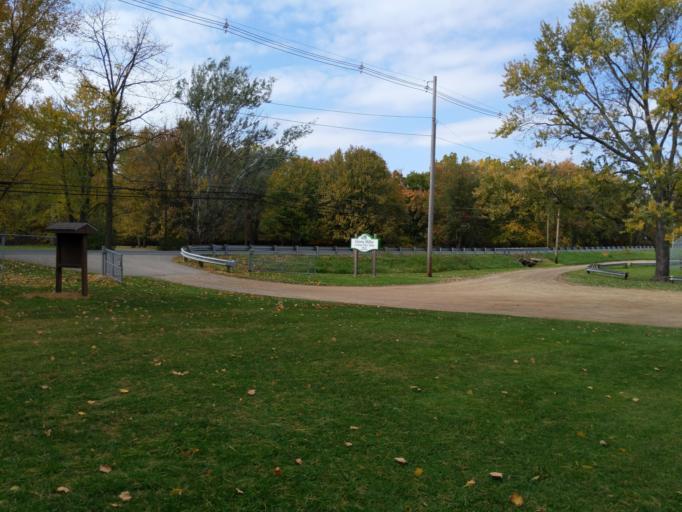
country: US
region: Michigan
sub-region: Clinton County
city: Wacousta
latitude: 42.8213
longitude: -84.7005
